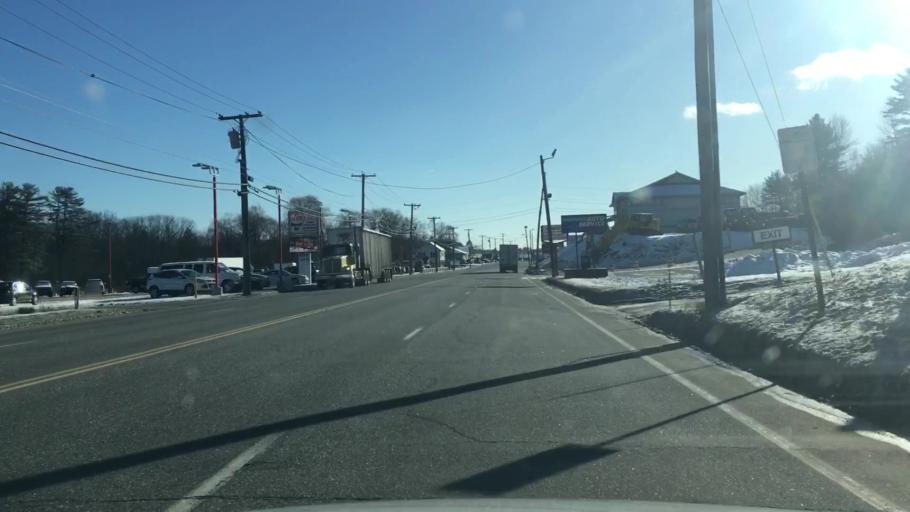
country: US
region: Maine
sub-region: Androscoggin County
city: Lewiston
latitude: 44.1395
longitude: -70.2262
